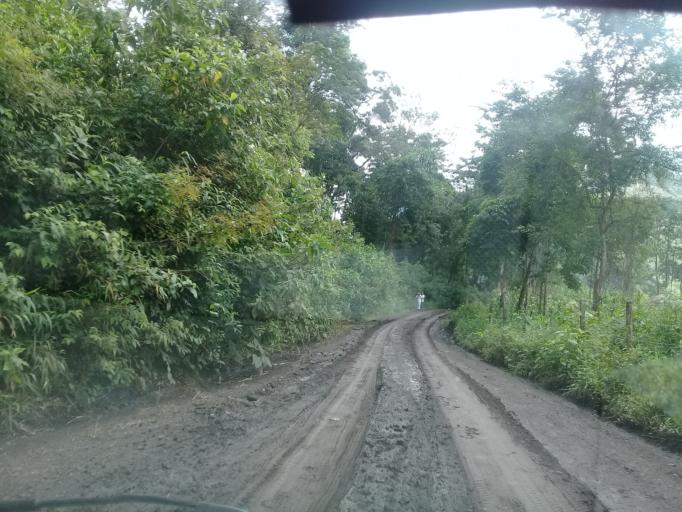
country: CO
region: Cundinamarca
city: Quipile
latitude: 4.7309
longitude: -74.5356
